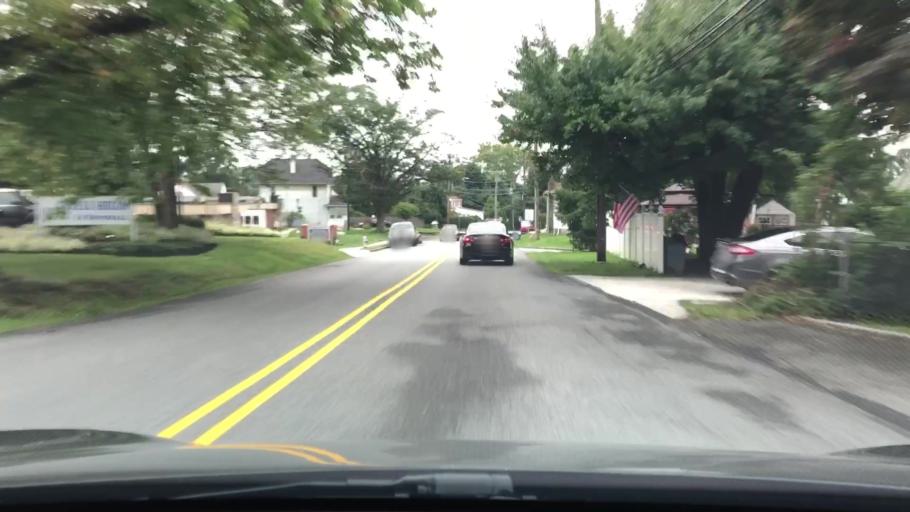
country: US
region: Pennsylvania
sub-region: Delaware County
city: Broomall
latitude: 39.9832
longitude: -75.3578
